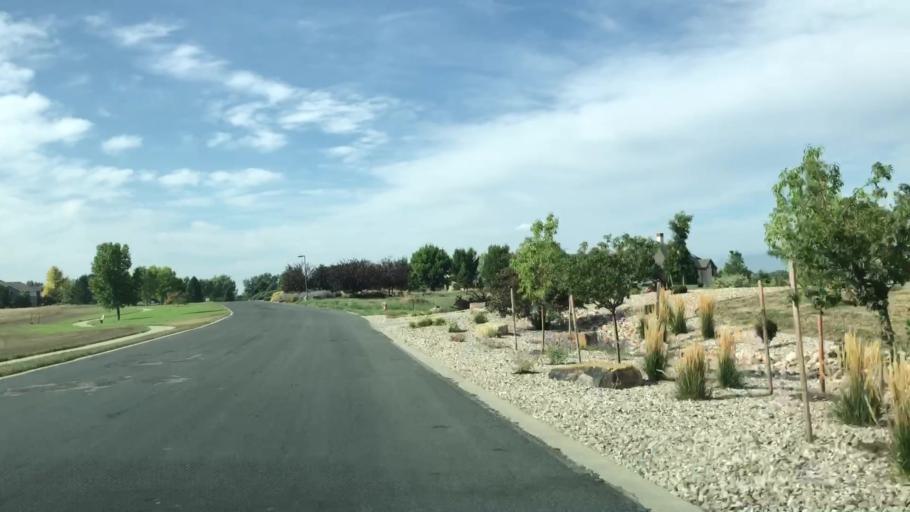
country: US
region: Colorado
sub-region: Larimer County
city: Loveland
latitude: 40.4352
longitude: -105.0553
